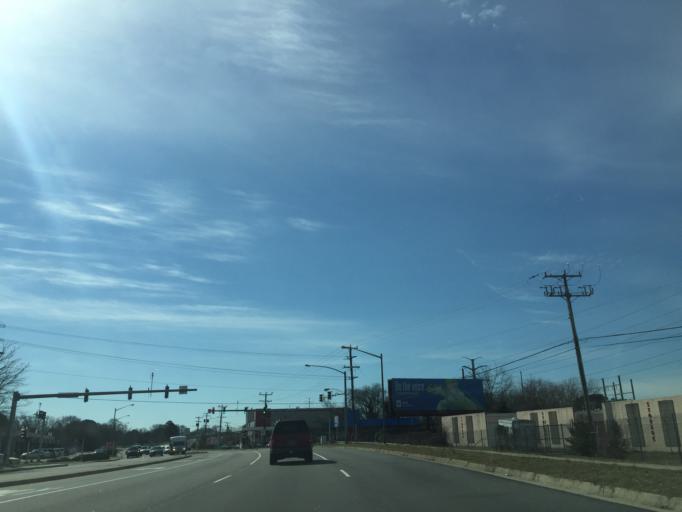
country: US
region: Virginia
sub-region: City of Norfolk
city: Norfolk
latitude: 36.9024
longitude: -76.2567
